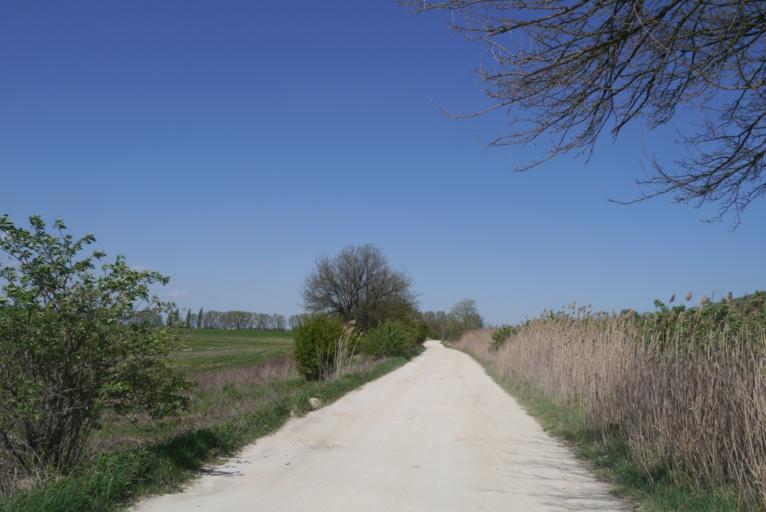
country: HU
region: Komarom-Esztergom
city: Kesztolc
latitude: 47.6941
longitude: 18.7991
